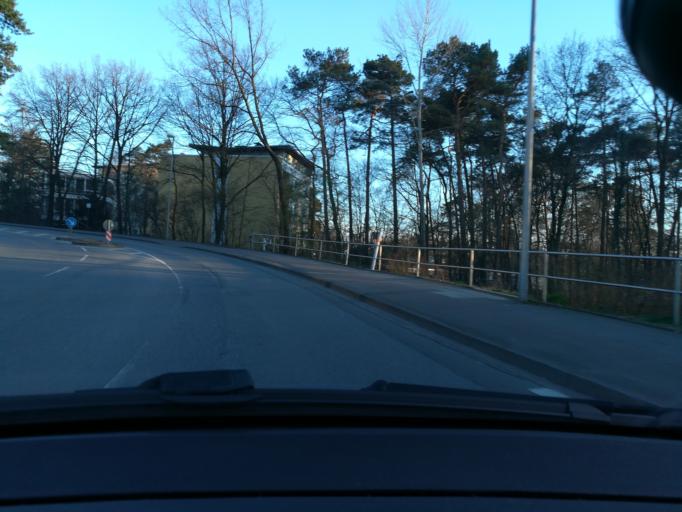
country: DE
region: North Rhine-Westphalia
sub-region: Regierungsbezirk Detmold
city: Oerlinghausen
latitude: 51.9437
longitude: 8.5818
